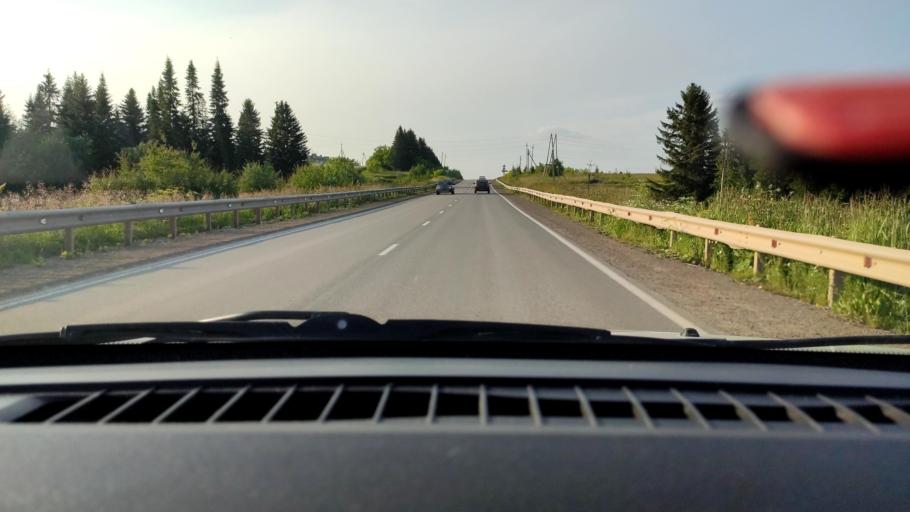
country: RU
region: Perm
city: Lobanovo
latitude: 57.8562
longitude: 56.2960
